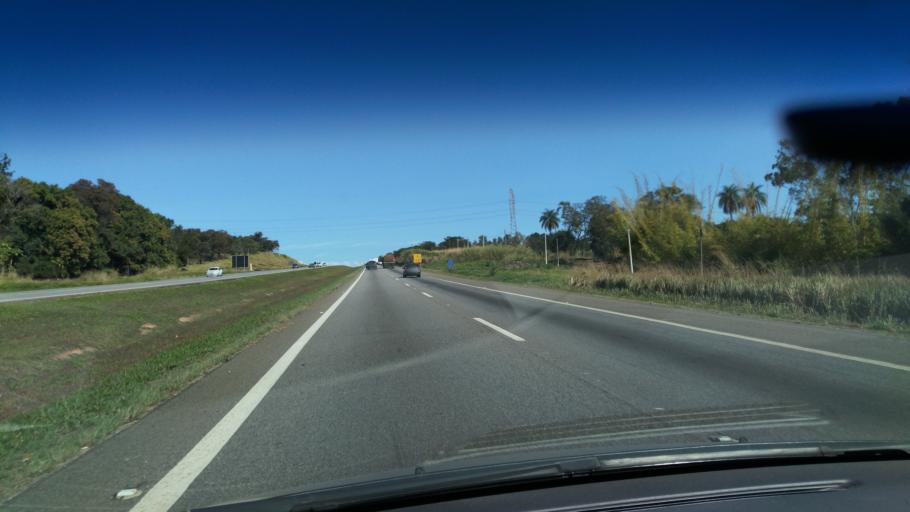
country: BR
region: Sao Paulo
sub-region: Jaguariuna
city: Jaguariuna
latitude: -22.7386
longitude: -47.0181
